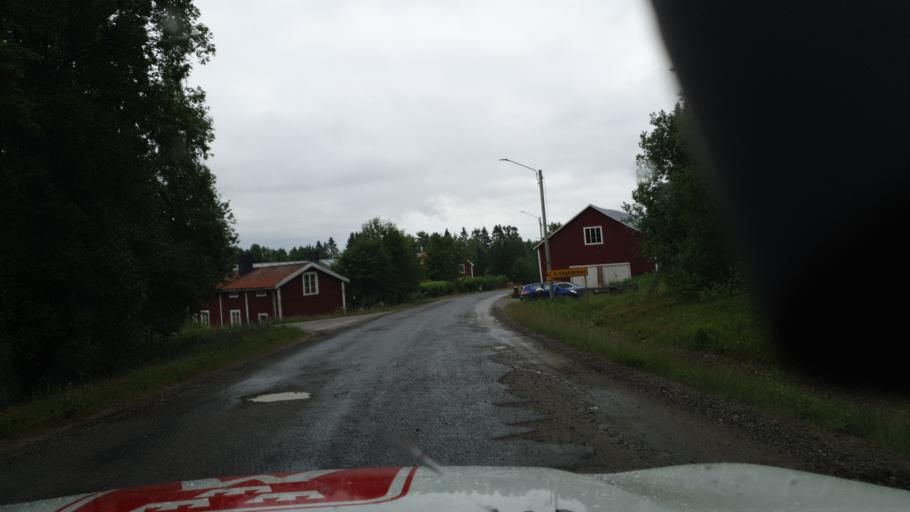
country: SE
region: Vaesterbotten
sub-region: Vannas Kommun
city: Vaennaes
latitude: 63.7855
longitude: 19.8357
